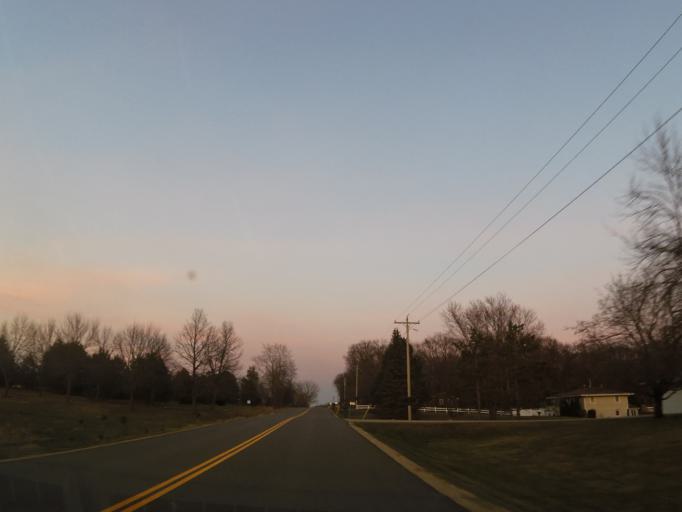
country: US
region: Minnesota
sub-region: Scott County
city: Prior Lake
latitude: 44.6885
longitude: -93.4669
